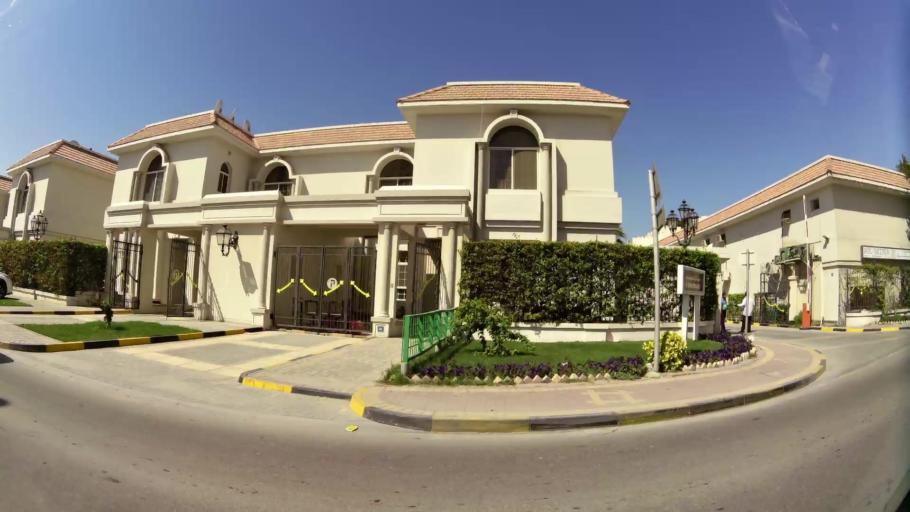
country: BH
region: Manama
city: Manama
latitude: 26.2061
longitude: 50.5918
